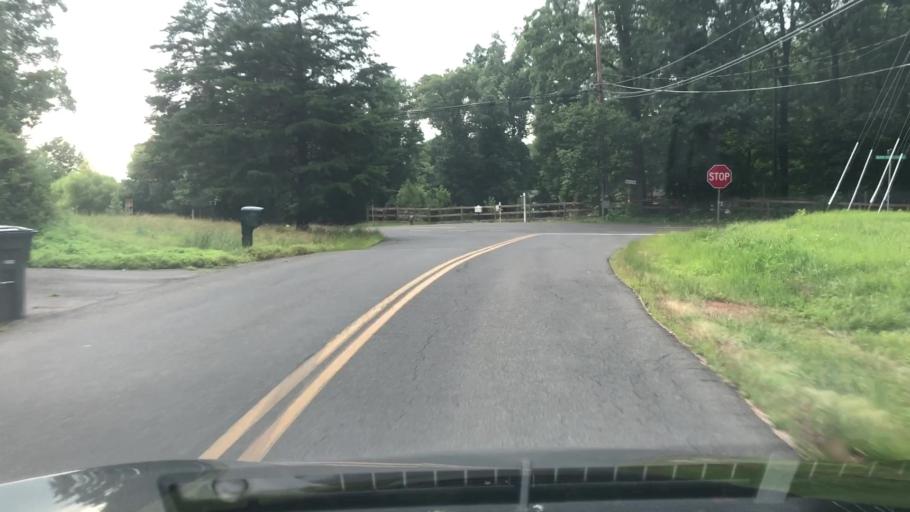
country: US
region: Virginia
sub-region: Fauquier County
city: New Baltimore
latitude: 38.7600
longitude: -77.6926
